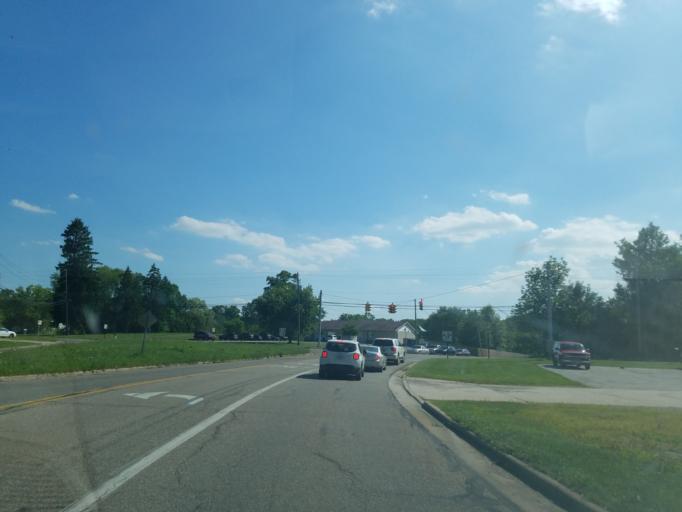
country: US
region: Ohio
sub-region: Portage County
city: Ravenna
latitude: 41.1743
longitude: -81.2631
